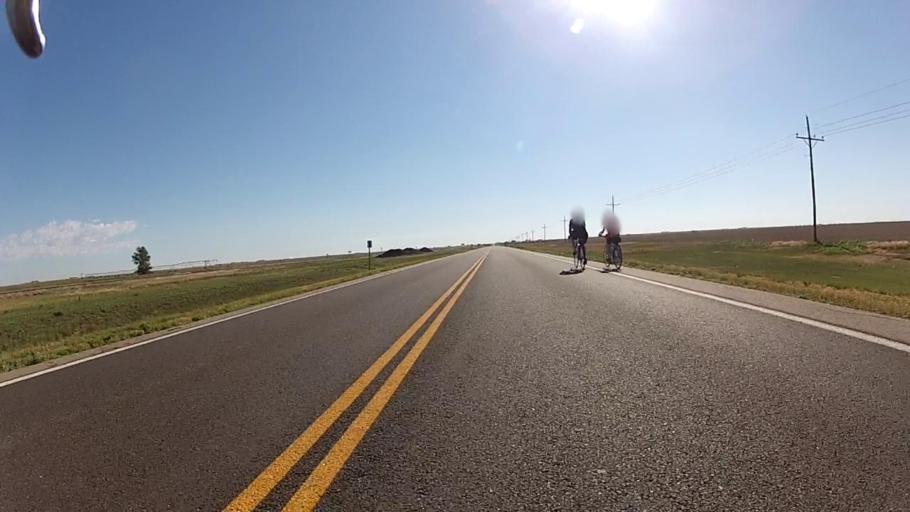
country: US
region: Kansas
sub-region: Haskell County
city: Sublette
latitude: 37.5609
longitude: -100.5675
